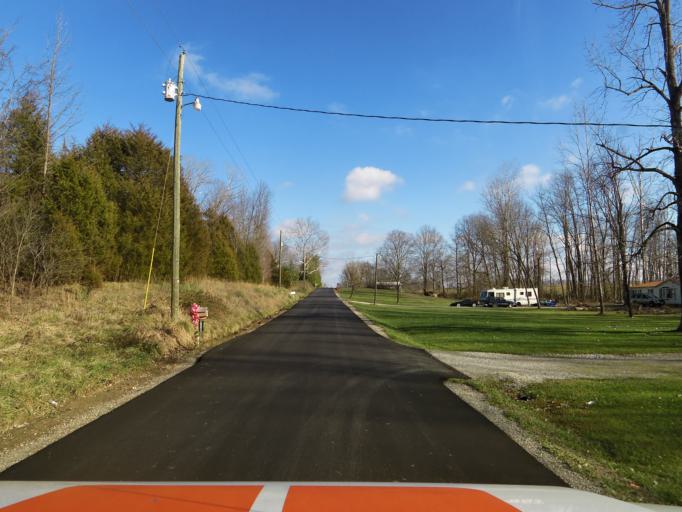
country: US
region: Indiana
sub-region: Jennings County
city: Country Squire Lakes
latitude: 38.9832
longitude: -85.7799
